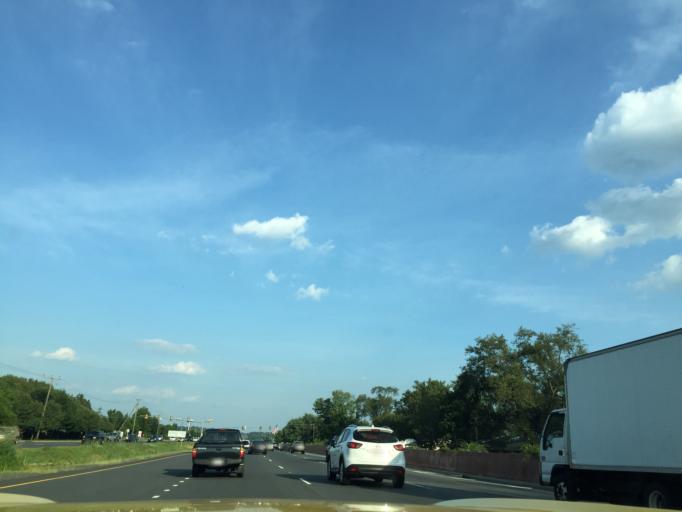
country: US
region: Virginia
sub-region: Loudoun County
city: Sugarland Run
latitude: 39.0204
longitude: -77.3829
